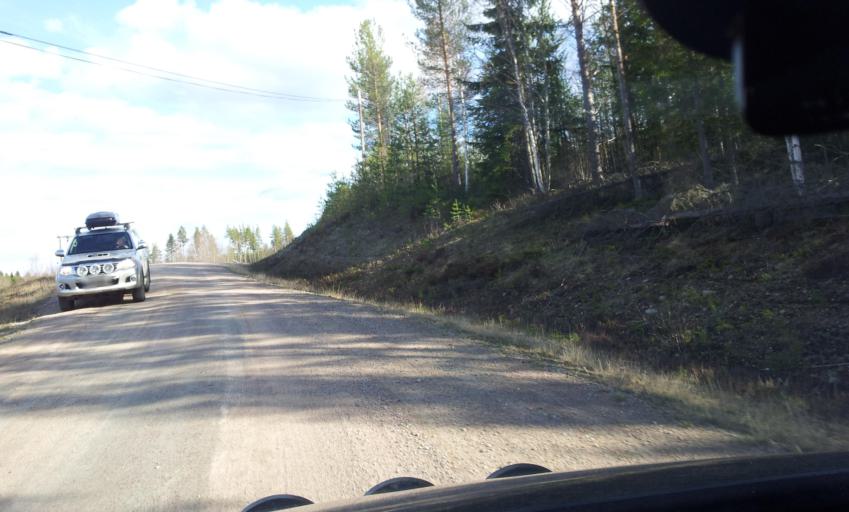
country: SE
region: Vaesternorrland
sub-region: Ange Kommun
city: Ange
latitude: 62.1779
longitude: 15.6325
